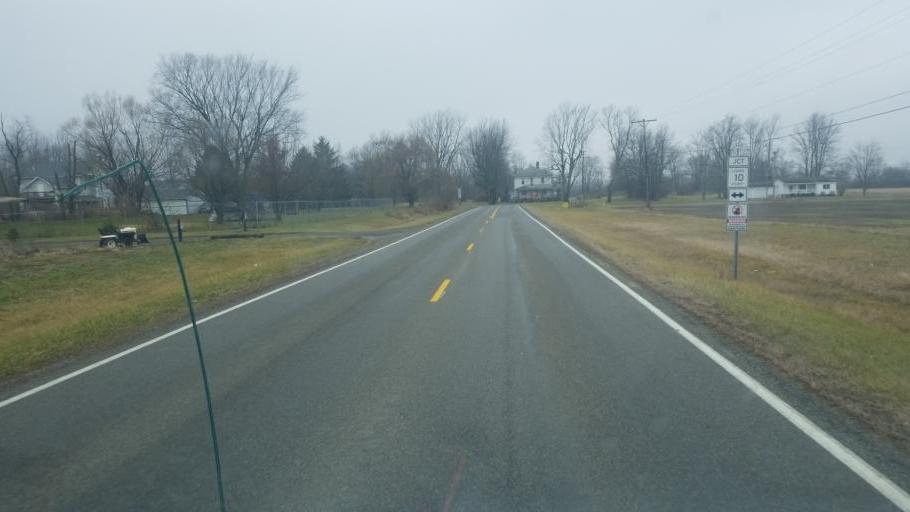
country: US
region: Ohio
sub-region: Champaign County
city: North Lewisburg
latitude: 40.3323
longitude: -83.5760
